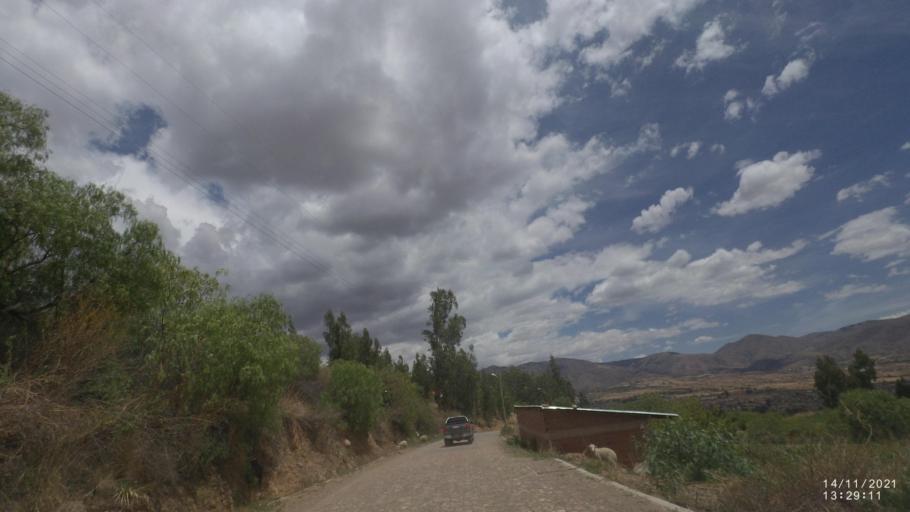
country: BO
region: Cochabamba
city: Colomi
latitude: -17.3881
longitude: -65.9844
